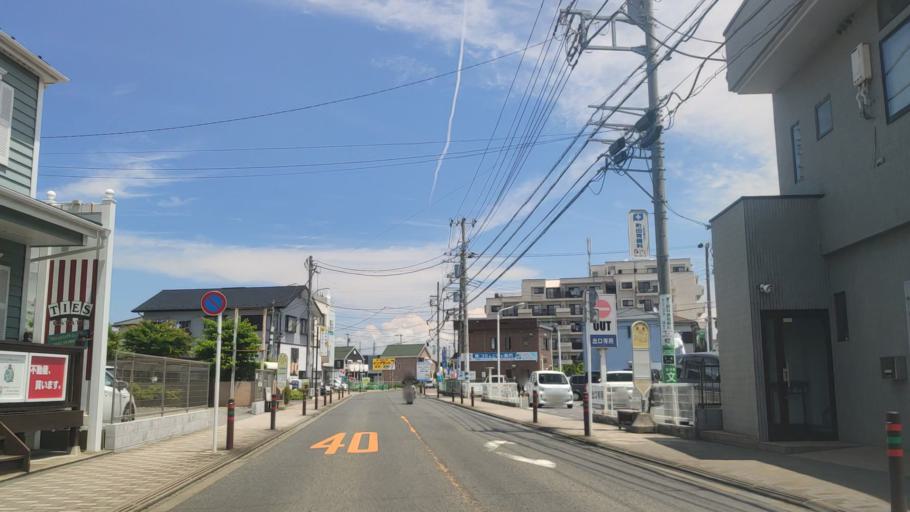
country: JP
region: Kanagawa
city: Chigasaki
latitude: 35.3367
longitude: 139.3936
